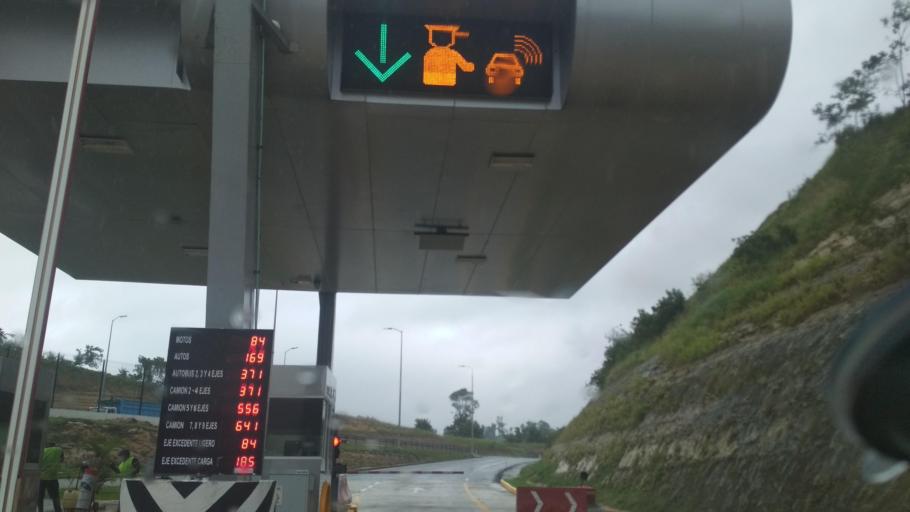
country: MX
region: Veracruz
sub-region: Papantla
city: Polutla
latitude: 20.4591
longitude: -97.2467
